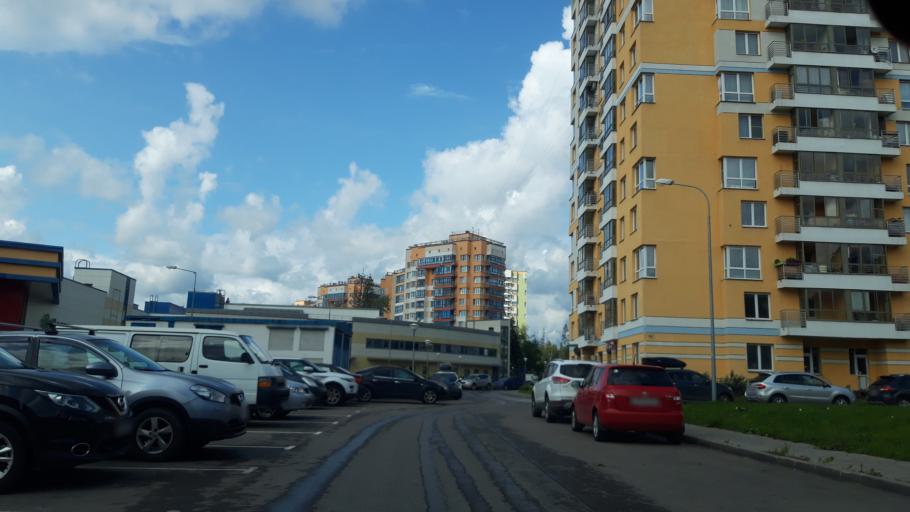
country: RU
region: Moscow
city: Zelenograd
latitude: 55.9640
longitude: 37.1879
